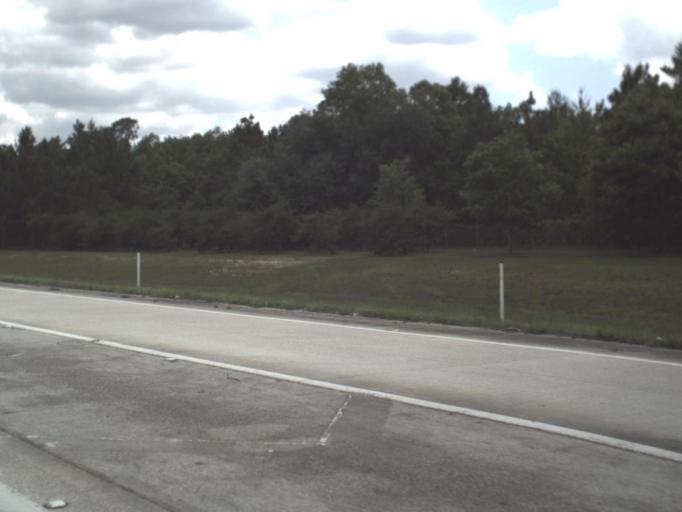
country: US
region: Florida
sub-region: Saint Johns County
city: Palm Valley
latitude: 30.2120
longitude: -81.5141
